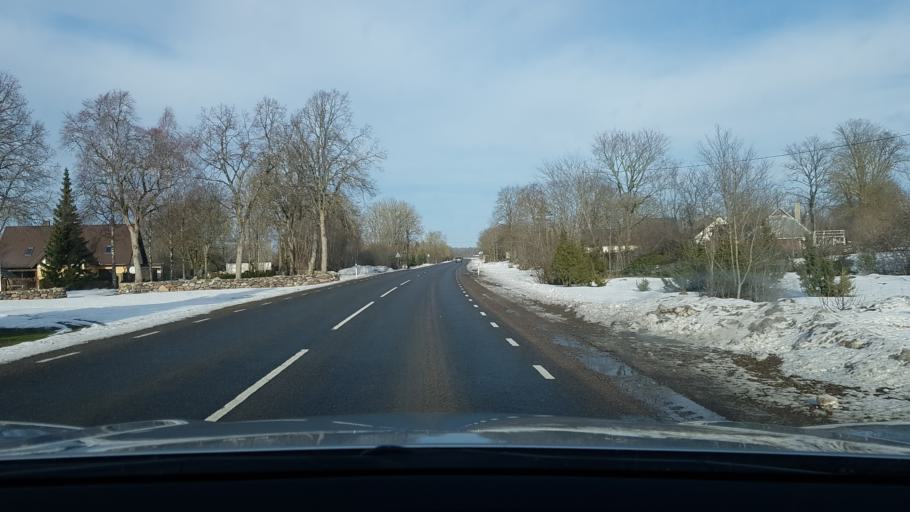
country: EE
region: Saare
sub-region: Kuressaare linn
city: Kuressaare
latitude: 58.2898
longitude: 22.5399
